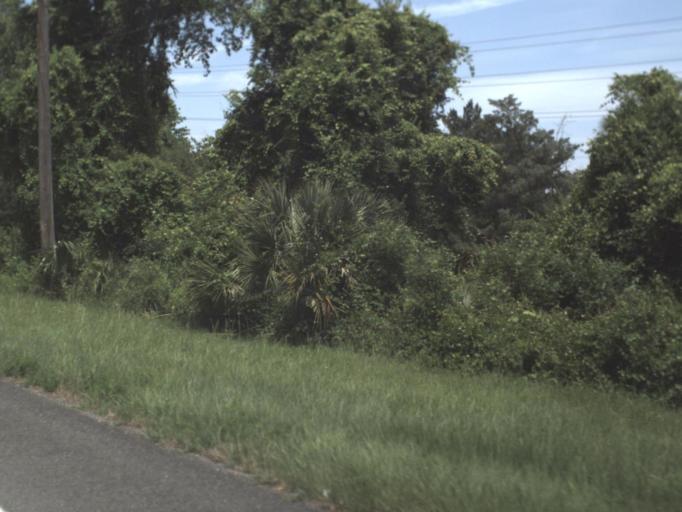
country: US
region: Florida
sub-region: Nassau County
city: Yulee
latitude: 30.5706
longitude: -81.6118
